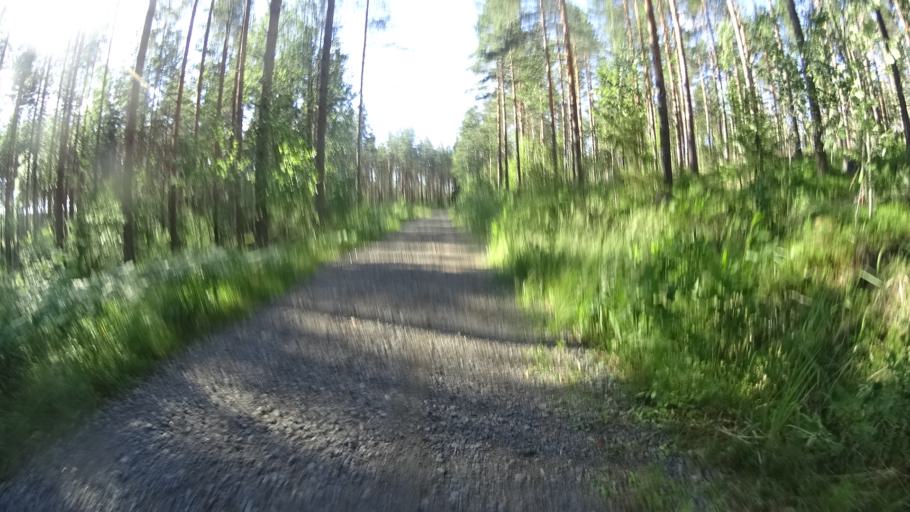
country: FI
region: Uusimaa
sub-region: Helsinki
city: Karkkila
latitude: 60.6492
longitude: 24.1617
